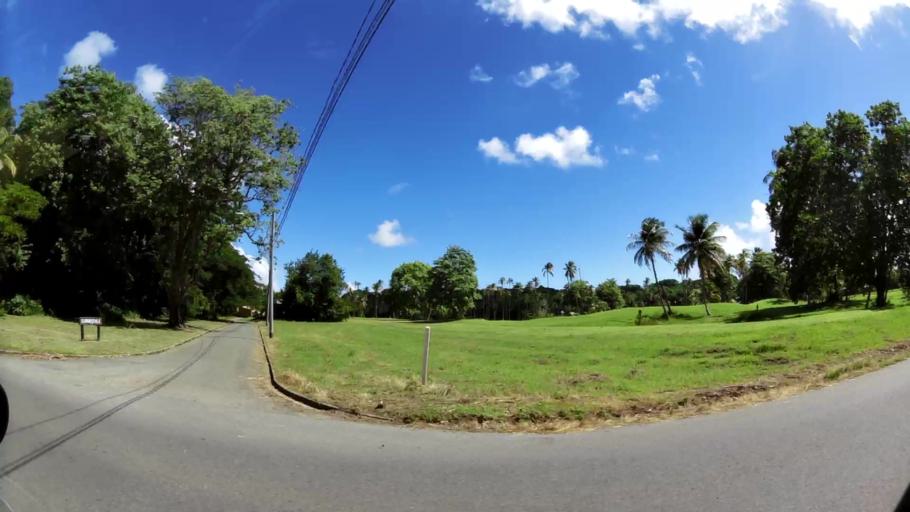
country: TT
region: Tobago
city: Scarborough
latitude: 11.1851
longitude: -60.7989
